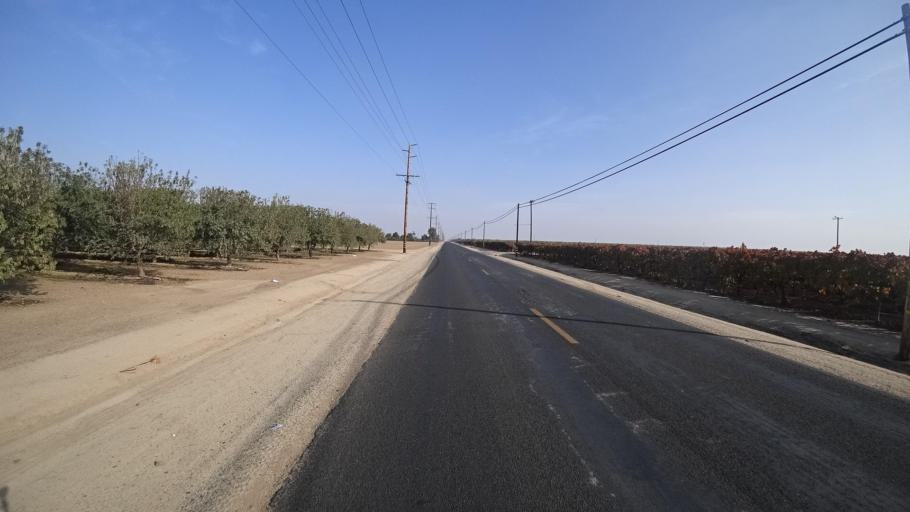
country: US
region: California
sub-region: Tulare County
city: Richgrove
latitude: 35.7761
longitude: -119.1480
